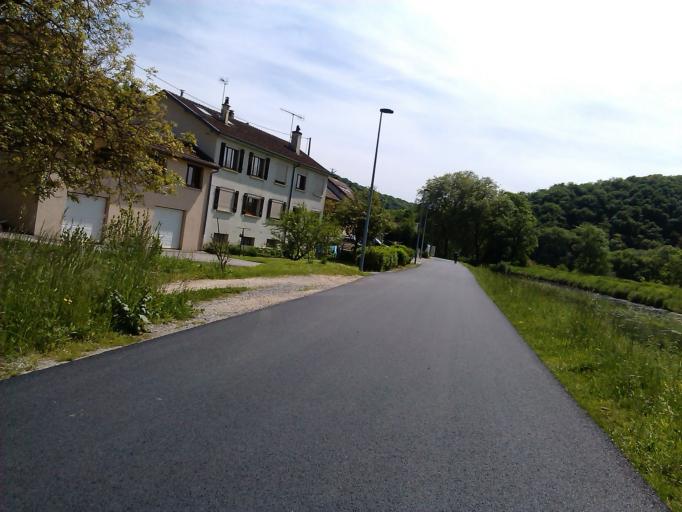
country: FR
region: Franche-Comte
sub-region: Departement du Doubs
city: Avanne-Aveney
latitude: 47.1961
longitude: 5.9592
